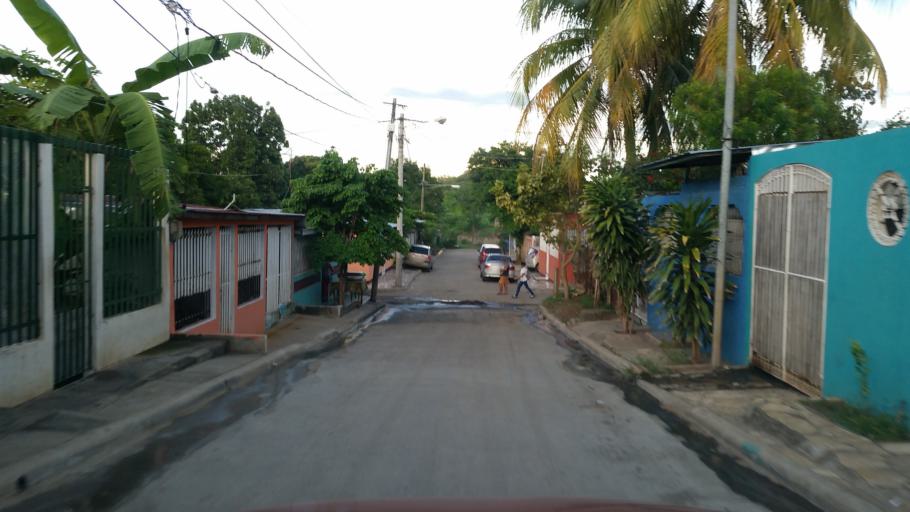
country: NI
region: Managua
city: Managua
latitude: 12.1178
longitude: -86.2828
